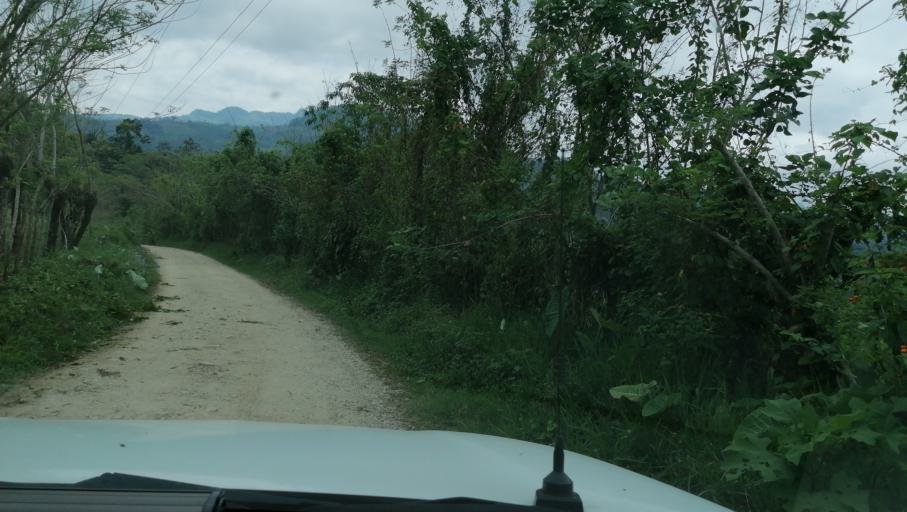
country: MX
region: Chiapas
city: Ocotepec
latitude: 17.2814
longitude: -93.2261
